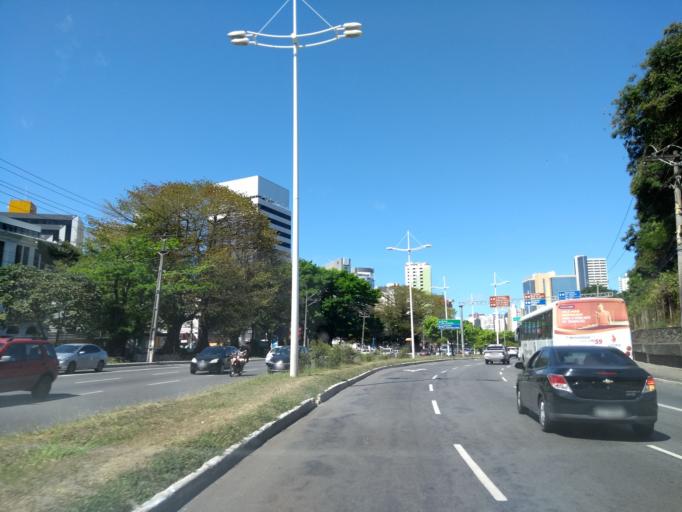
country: BR
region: Bahia
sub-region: Salvador
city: Salvador
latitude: -12.9898
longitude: -38.4729
